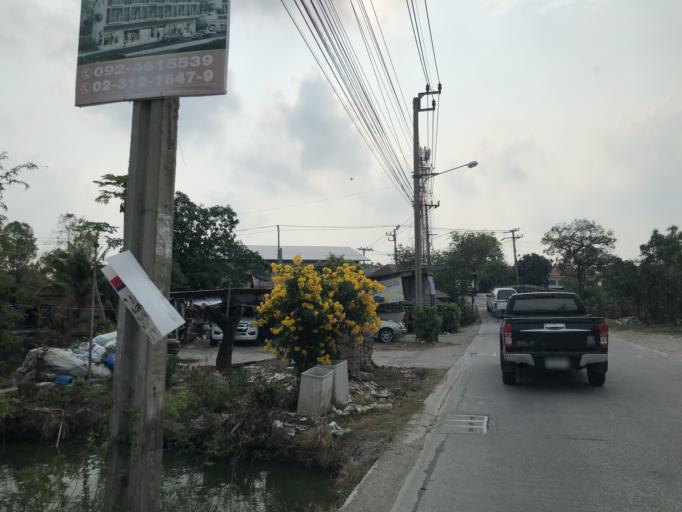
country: TH
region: Bangkok
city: Bang Na
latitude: 13.5845
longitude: 100.7077
